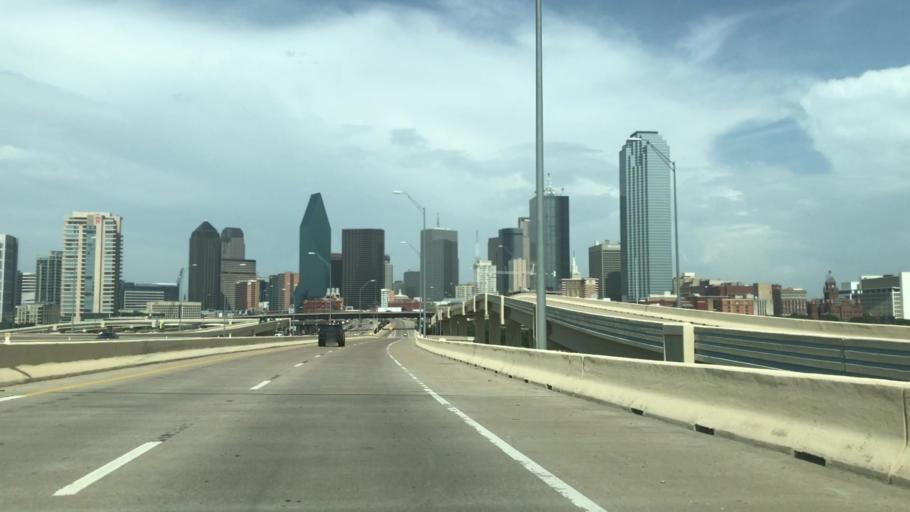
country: US
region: Texas
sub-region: Dallas County
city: Dallas
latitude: 32.7813
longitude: -96.8177
